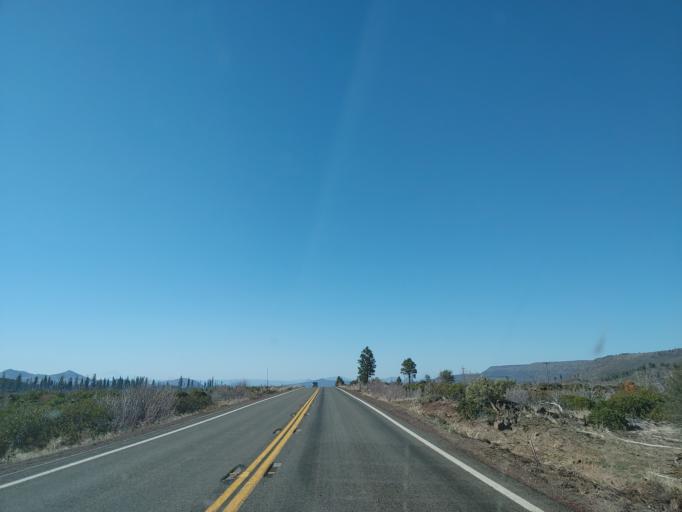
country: US
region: California
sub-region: Shasta County
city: Burney
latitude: 40.7044
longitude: -121.4183
